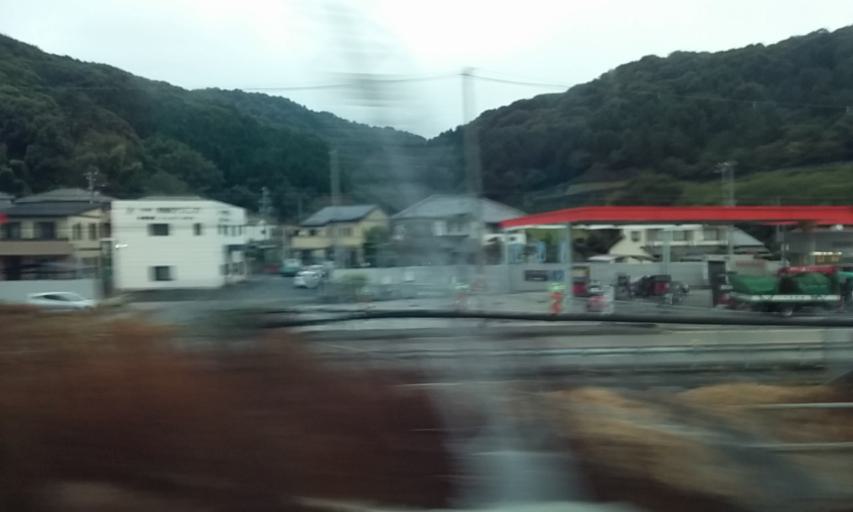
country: JP
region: Hyogo
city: Tatsunocho-tominaga
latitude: 34.8292
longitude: 134.6142
